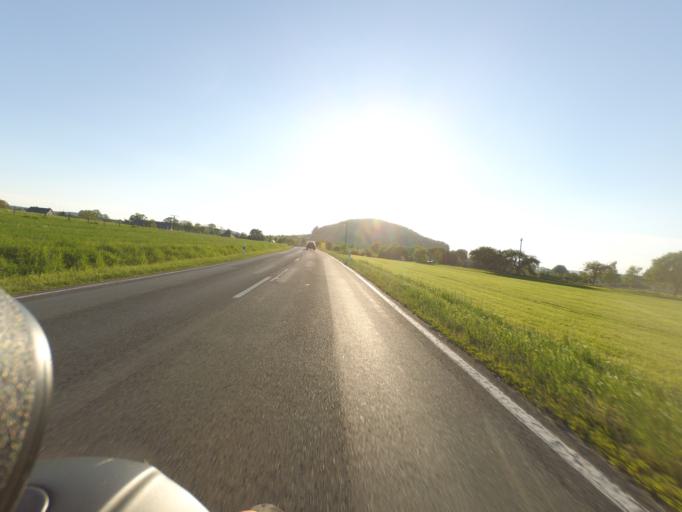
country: DE
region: Saxony
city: Reinhardtsgrimma
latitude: 50.8663
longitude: 13.7420
